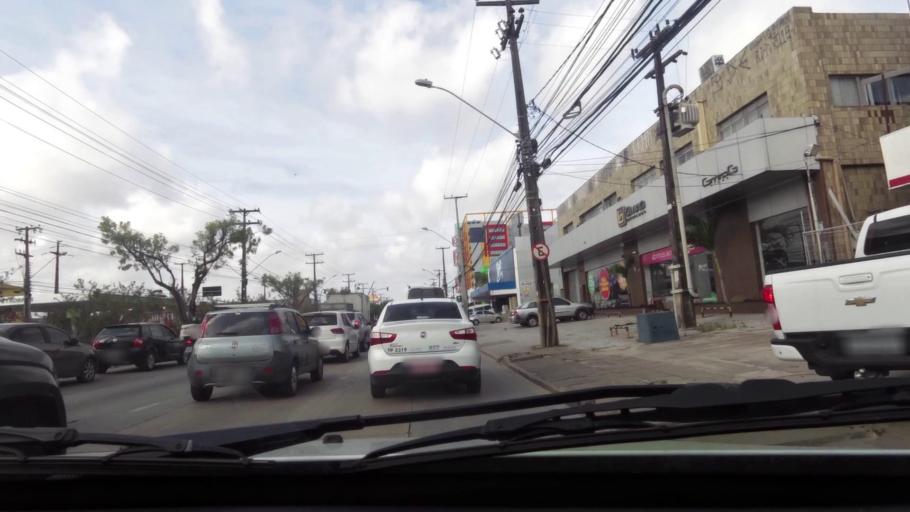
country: BR
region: Pernambuco
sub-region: Recife
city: Recife
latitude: -8.1049
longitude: -34.9111
